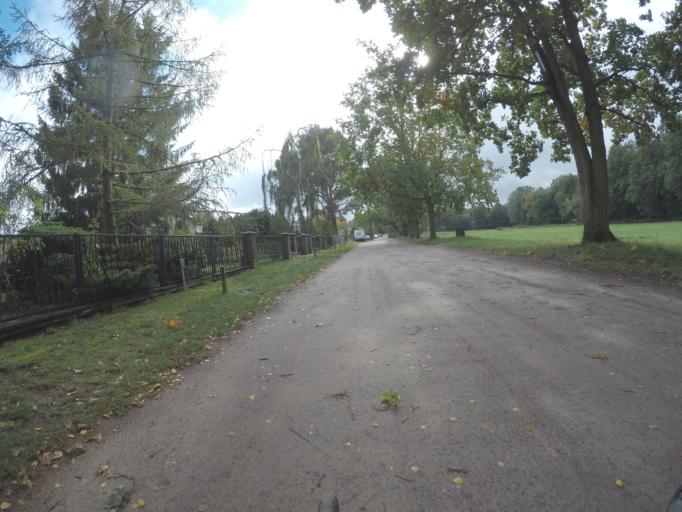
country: DE
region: Berlin
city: Blankenfelde
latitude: 52.6391
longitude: 13.3724
